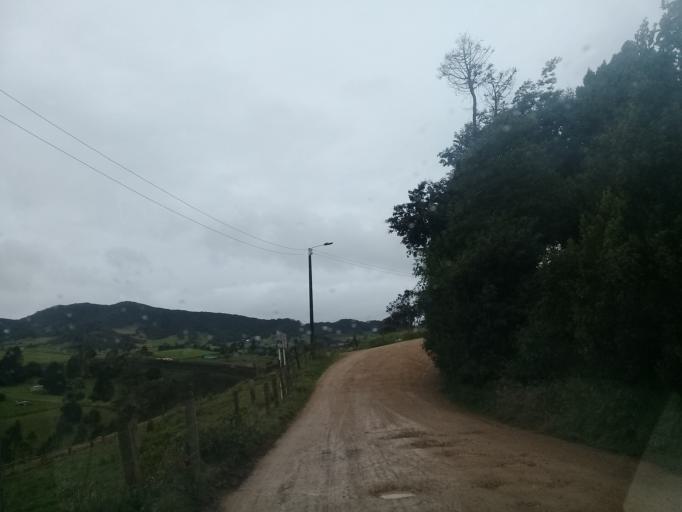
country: CO
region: Boyaca
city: Samaca
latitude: 5.4482
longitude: -73.4361
